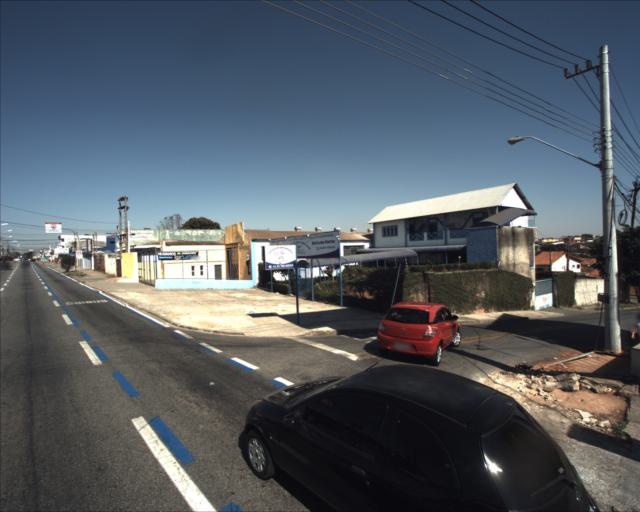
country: BR
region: Sao Paulo
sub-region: Sorocaba
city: Sorocaba
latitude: -23.4686
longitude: -47.4780
